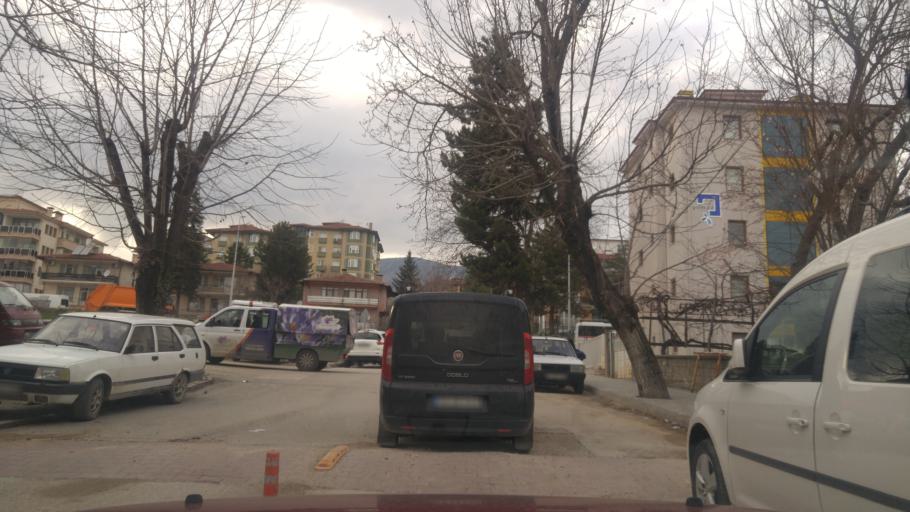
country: TR
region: Karabuk
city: Safranbolu
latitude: 41.2564
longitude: 32.6785
